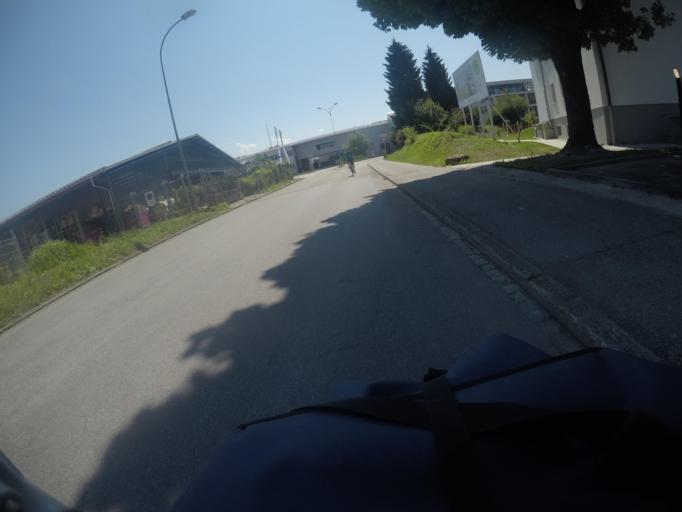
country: CH
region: Saint Gallen
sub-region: Wahlkreis Rheintal
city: Sankt Margrethen
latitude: 47.4472
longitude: 9.6490
